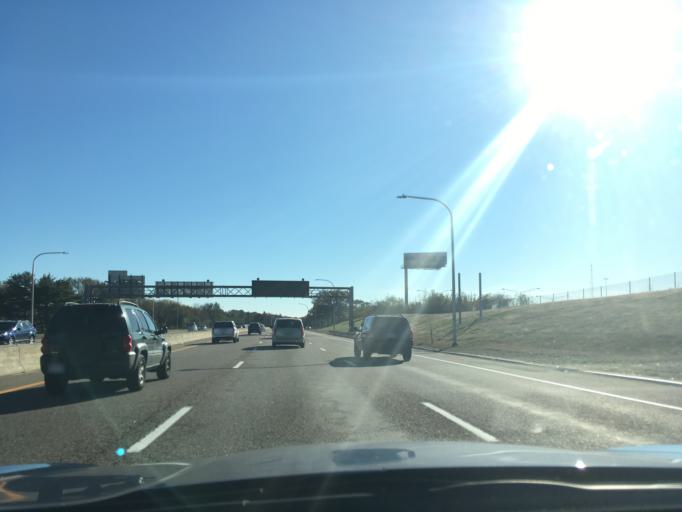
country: US
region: Rhode Island
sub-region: Providence County
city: Pawtucket
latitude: 41.8620
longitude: -71.4046
